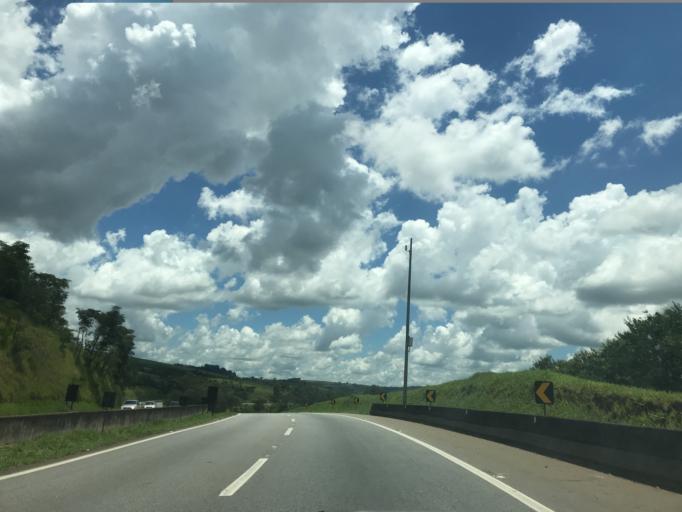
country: BR
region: Minas Gerais
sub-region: Nepomuceno
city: Nepomuceno
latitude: -21.4289
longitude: -45.2106
